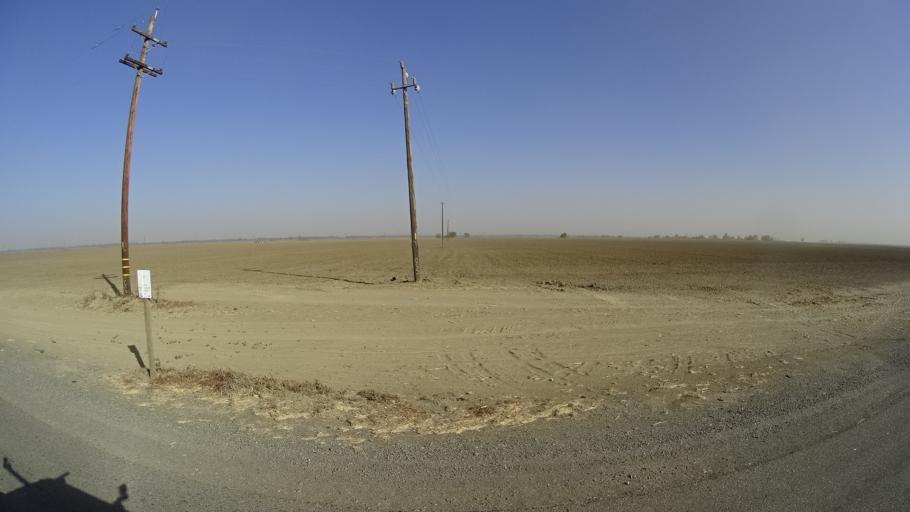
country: US
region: California
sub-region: Yolo County
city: Woodland
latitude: 38.7561
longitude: -121.7291
